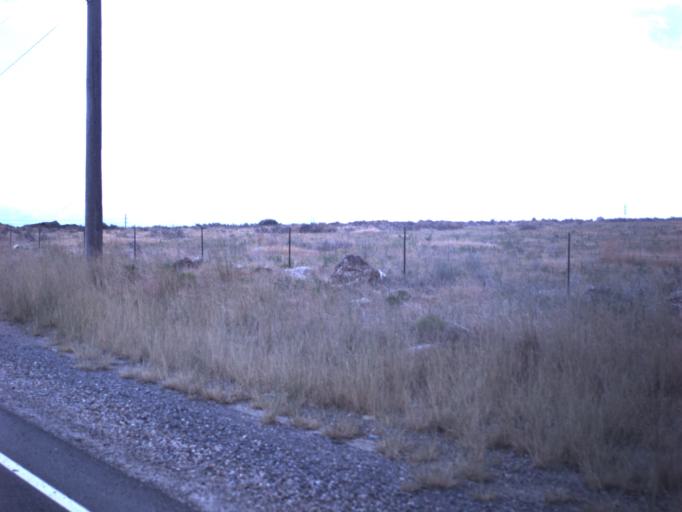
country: US
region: Utah
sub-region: Salt Lake County
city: Oquirrh
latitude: 40.6531
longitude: -112.0657
